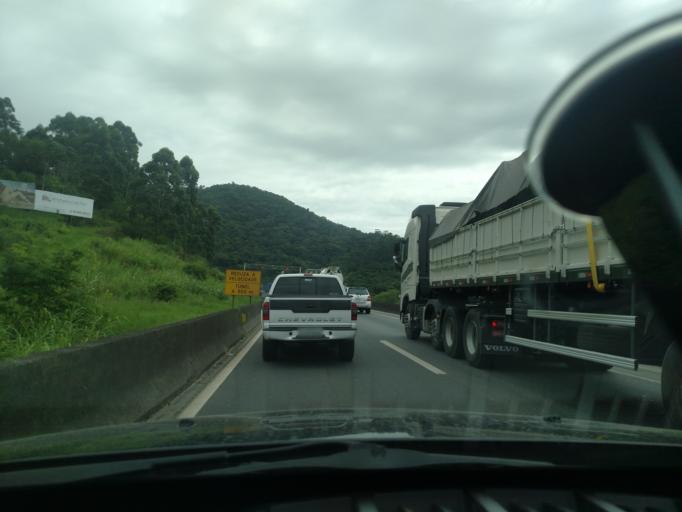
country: BR
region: Santa Catarina
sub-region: Itapema
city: Itapema
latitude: -27.0527
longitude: -48.5981
